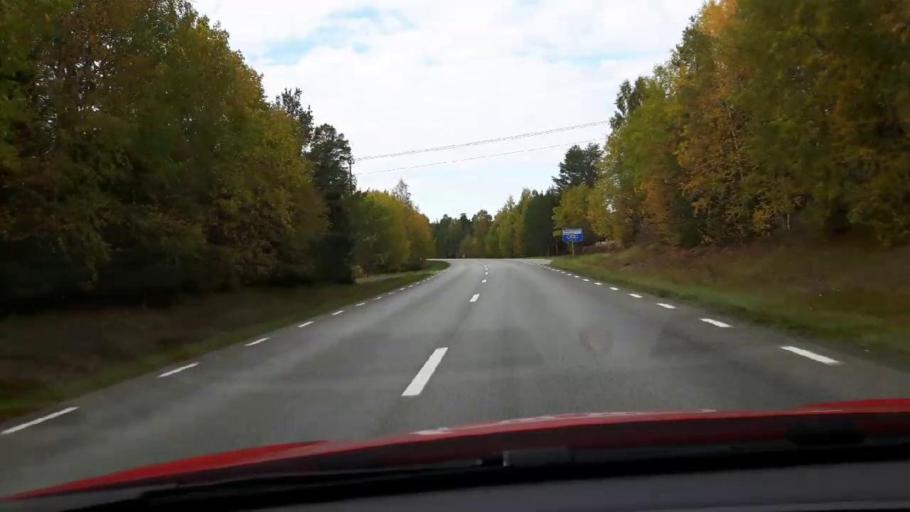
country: SE
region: Jaemtland
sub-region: Krokoms Kommun
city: Valla
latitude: 63.2543
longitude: 13.9952
